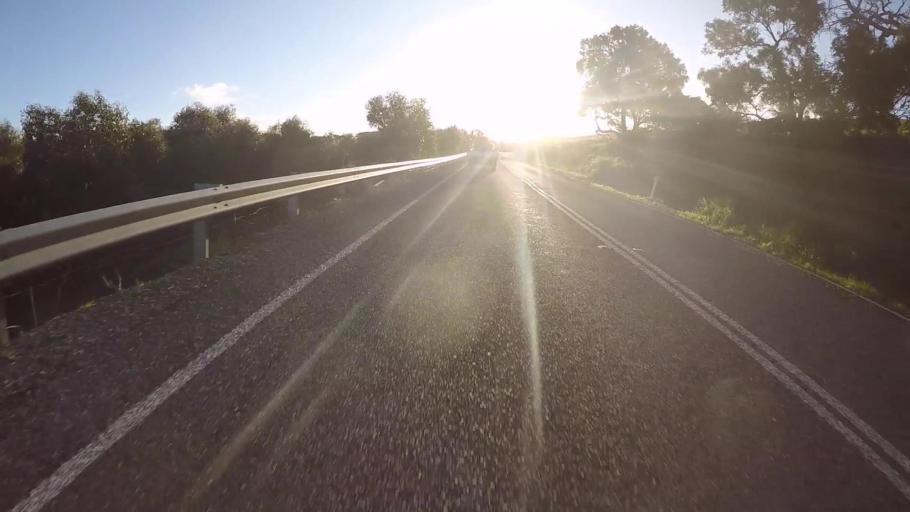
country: AU
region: Victoria
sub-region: Greater Geelong
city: Wandana Heights
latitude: -38.1715
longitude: 144.2350
